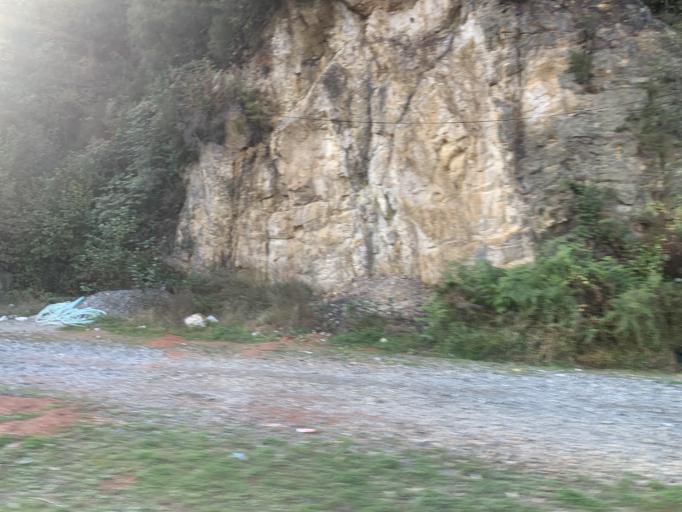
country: TR
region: Trabzon
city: Dernekpazari
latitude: 40.8303
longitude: 40.2691
